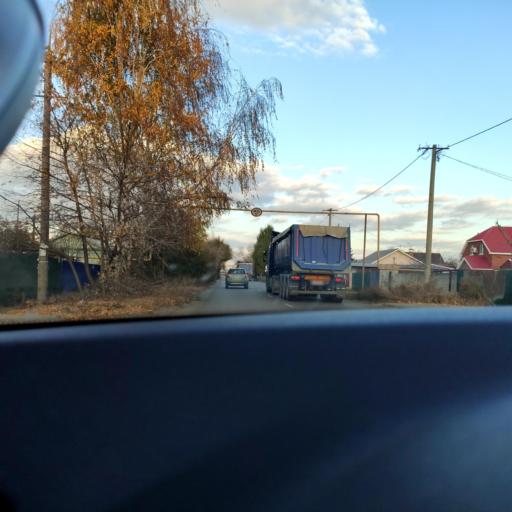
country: RU
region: Samara
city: Smyshlyayevka
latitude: 53.2404
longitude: 50.3330
